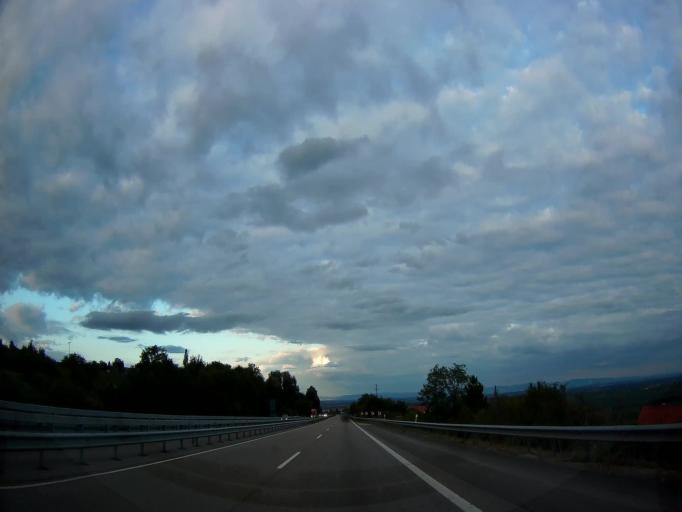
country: DE
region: Rheinland-Pfalz
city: Neuleiningen
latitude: 49.5432
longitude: 8.1335
